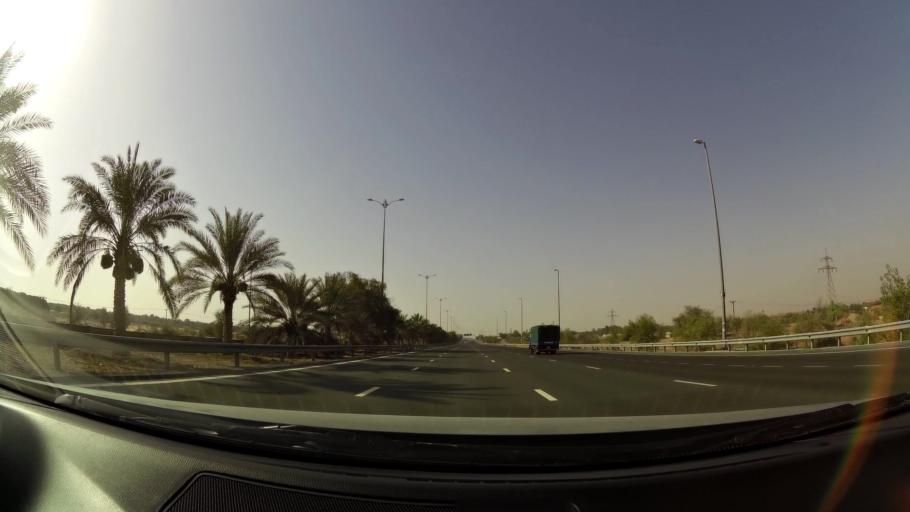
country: OM
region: Al Buraimi
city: Al Buraymi
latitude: 24.5674
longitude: 55.7491
